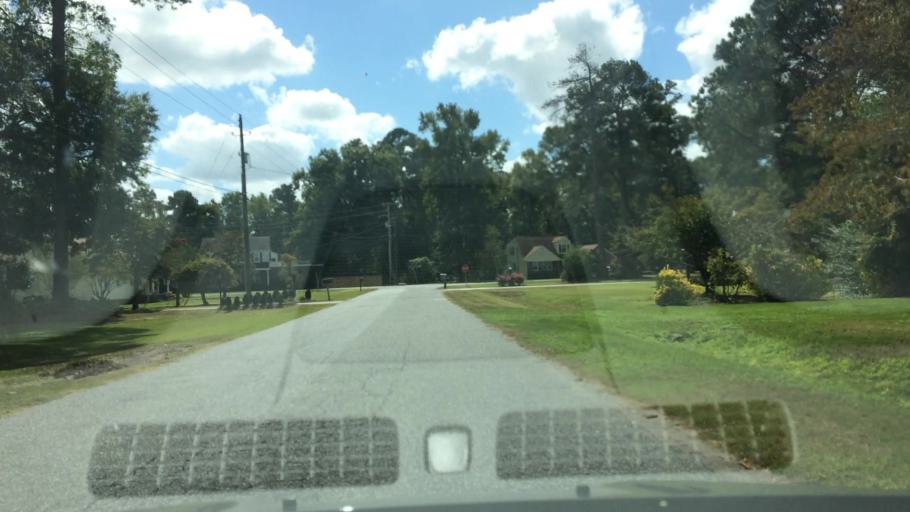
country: US
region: North Carolina
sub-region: Pitt County
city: Ayden
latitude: 35.4730
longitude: -77.4368
